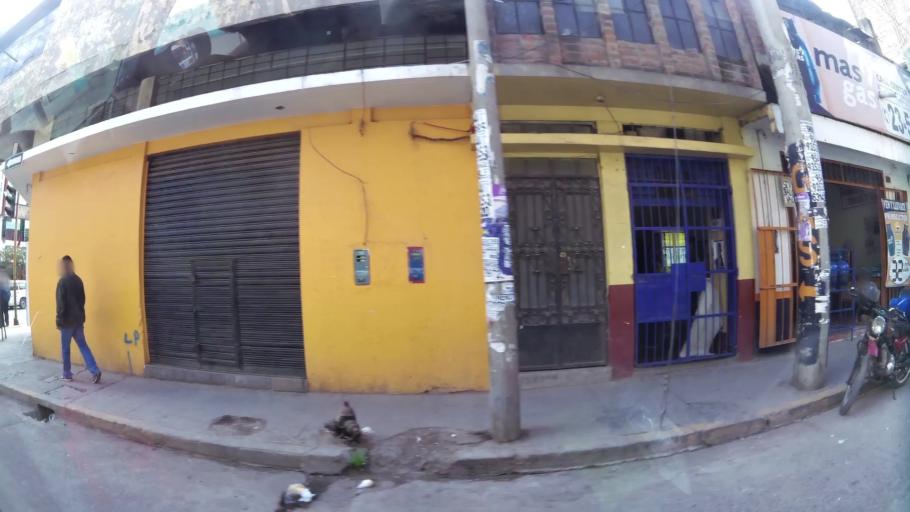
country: PE
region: Junin
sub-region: Provincia de Huancayo
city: Huancayo
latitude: -12.0748
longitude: -75.2063
